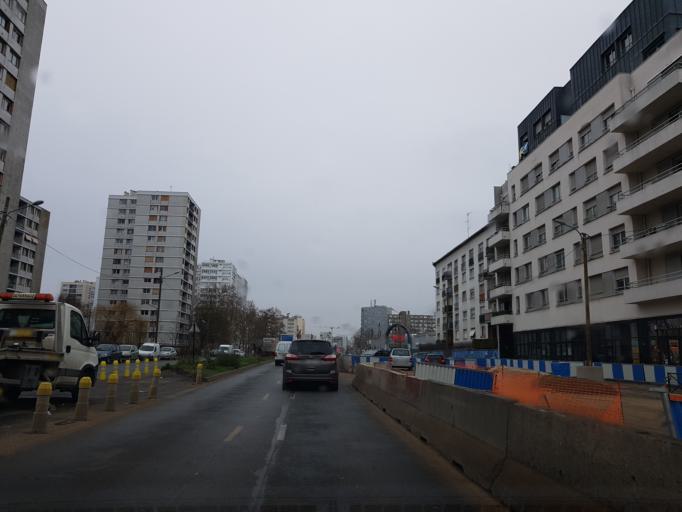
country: FR
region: Ile-de-France
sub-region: Departement du Val-de-Marne
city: Vitry-sur-Seine
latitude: 48.7874
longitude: 2.3908
